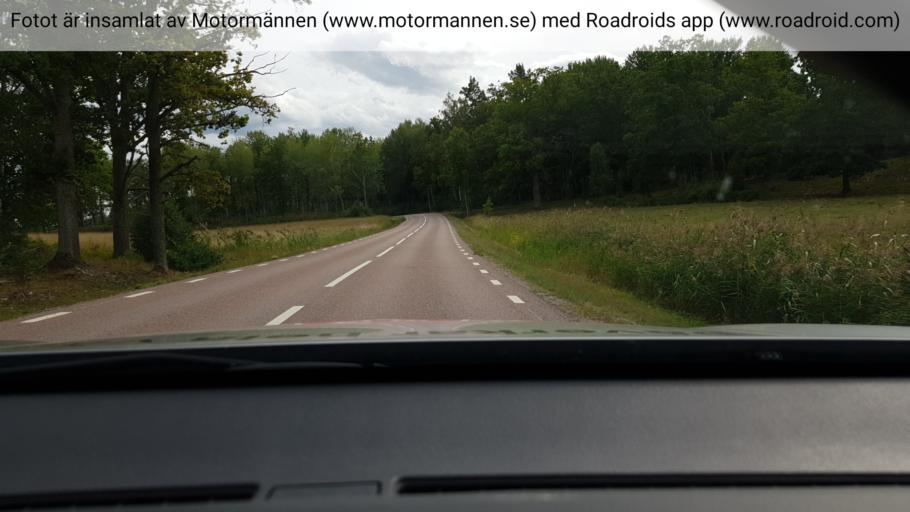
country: SE
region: Soedermanland
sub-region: Gnesta Kommun
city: Gnesta
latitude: 59.0318
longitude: 17.1647
